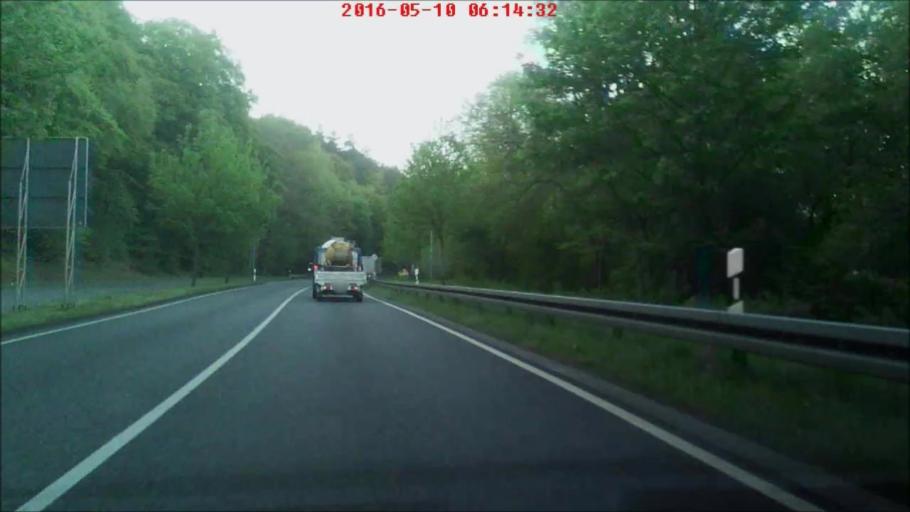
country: DE
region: Hesse
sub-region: Regierungsbezirk Kassel
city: Burghaun
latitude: 50.7599
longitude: 9.6862
